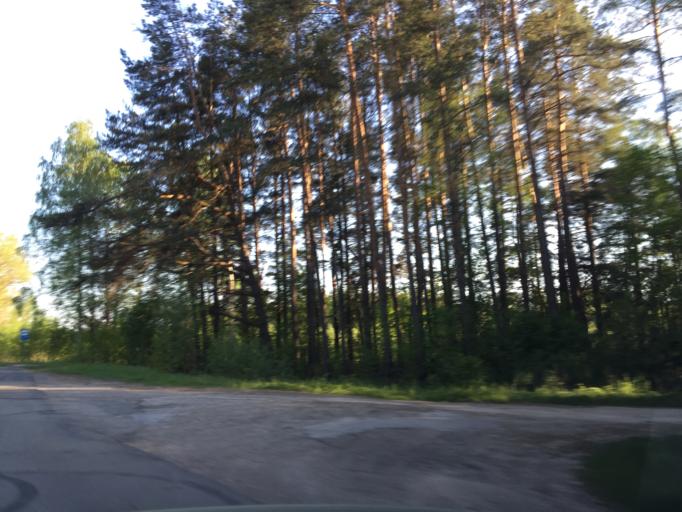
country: LV
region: Kekava
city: Kekava
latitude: 56.7800
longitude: 24.2998
